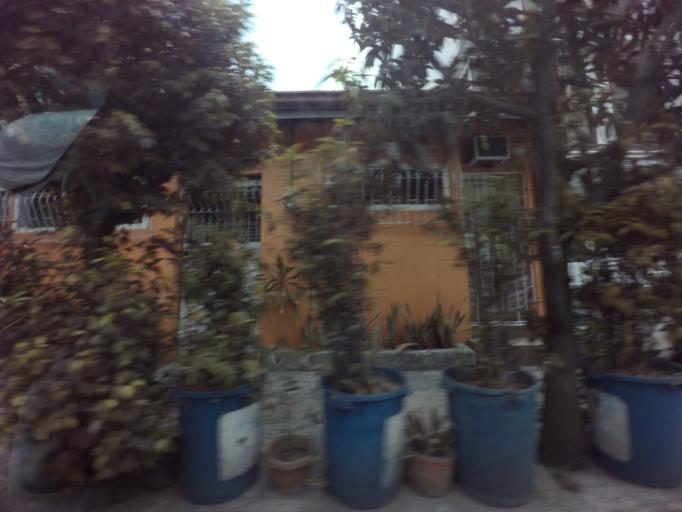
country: PH
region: Metro Manila
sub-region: Mandaluyong
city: Mandaluyong City
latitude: 14.5723
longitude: 121.0210
